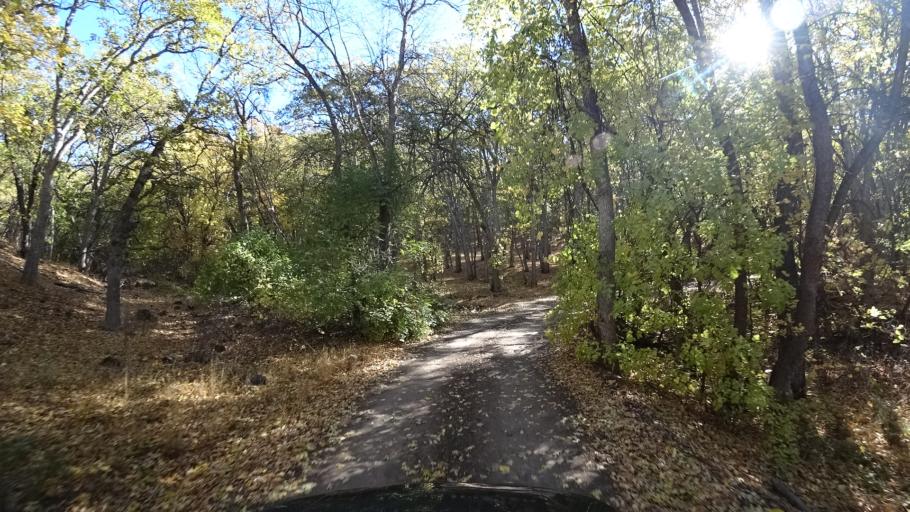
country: US
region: California
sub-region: Siskiyou County
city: Montague
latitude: 41.9846
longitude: -122.2969
